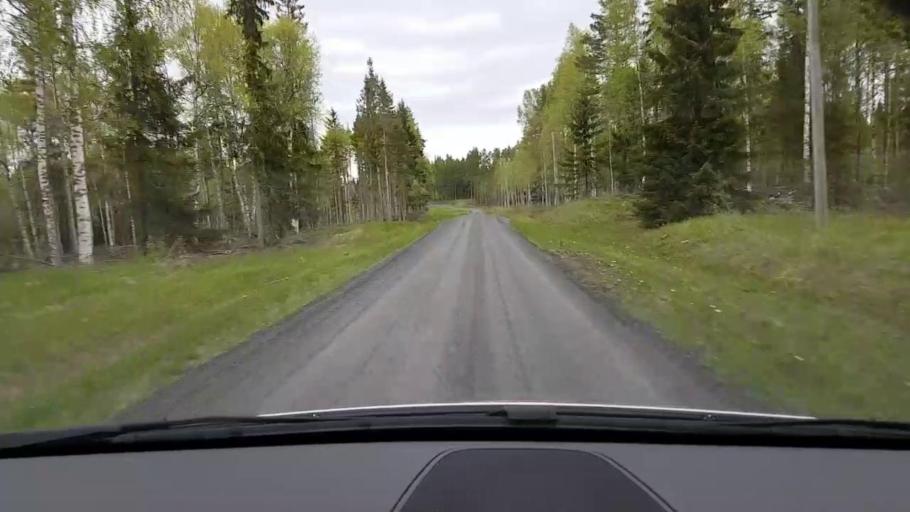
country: SE
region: Jaemtland
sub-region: Krokoms Kommun
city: Krokom
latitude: 63.2919
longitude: 14.3896
